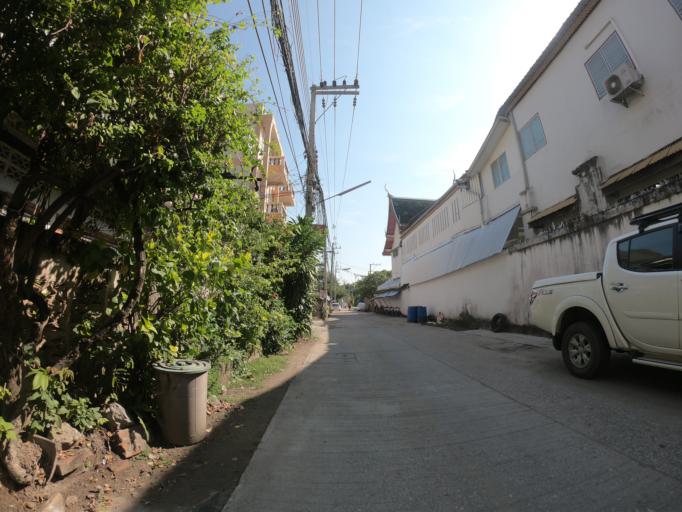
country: TH
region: Chiang Mai
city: Chiang Mai
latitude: 18.8030
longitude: 98.9888
